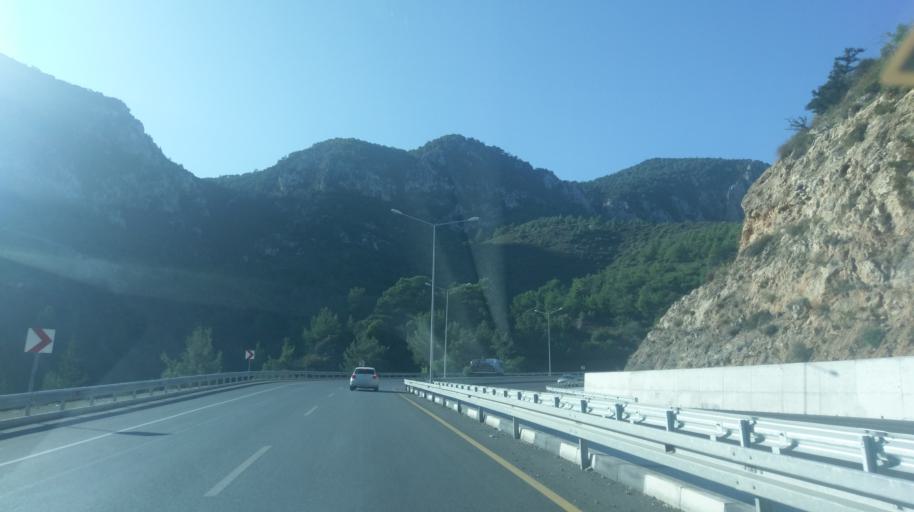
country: CY
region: Keryneia
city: Kyrenia
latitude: 35.3081
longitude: 33.3223
